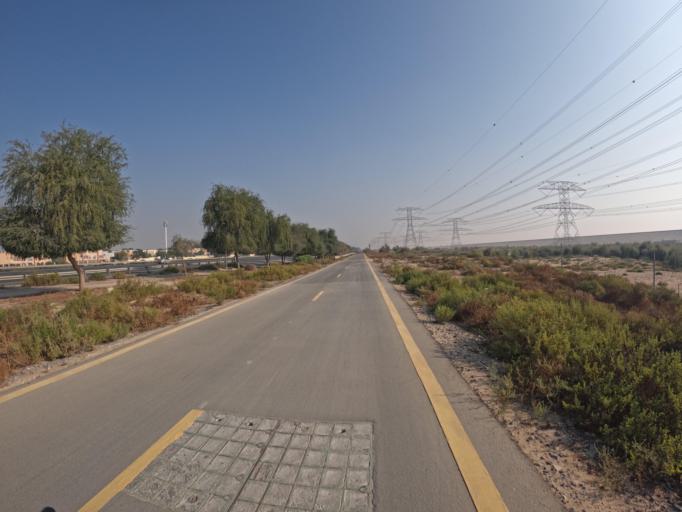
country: AE
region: Dubai
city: Dubai
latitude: 25.0247
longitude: 55.2848
